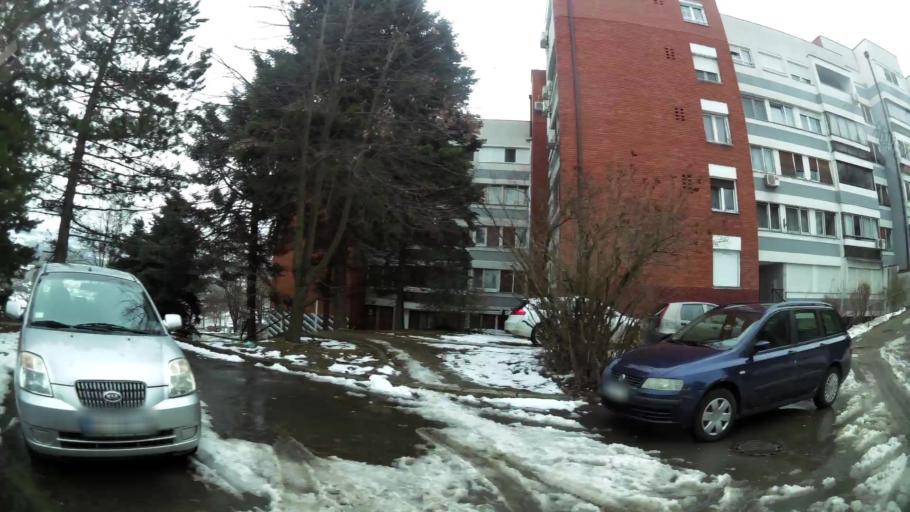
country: RS
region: Central Serbia
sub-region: Belgrade
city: Vozdovac
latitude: 44.7525
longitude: 20.5011
